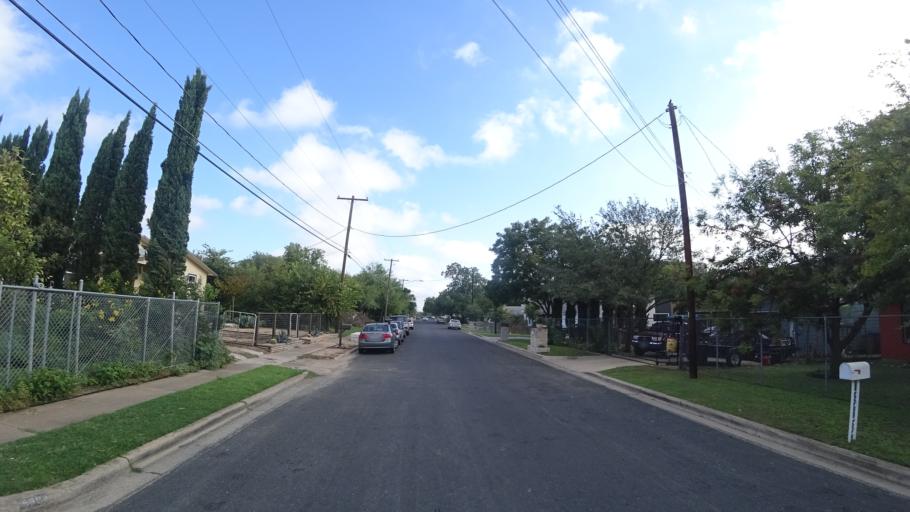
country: US
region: Texas
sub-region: Travis County
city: Austin
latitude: 30.3260
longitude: -97.6968
